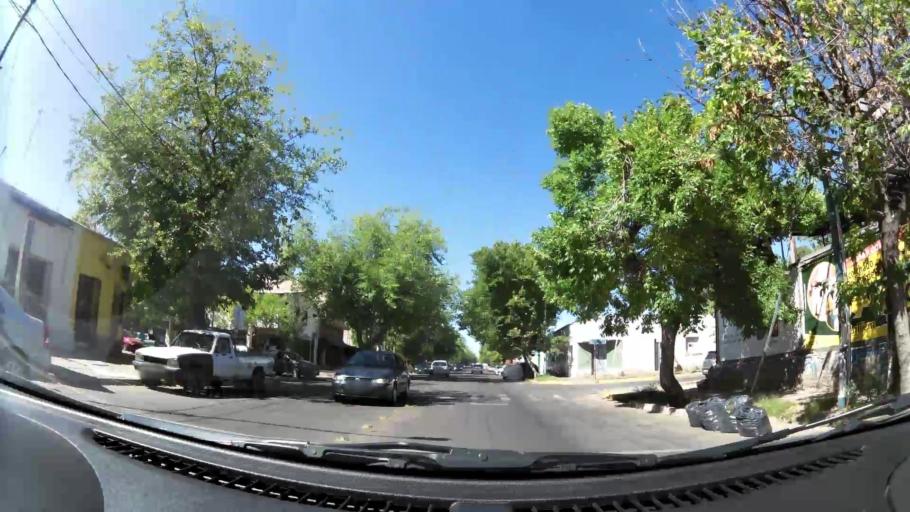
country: AR
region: Mendoza
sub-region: Departamento de Godoy Cruz
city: Godoy Cruz
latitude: -32.9114
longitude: -68.8601
